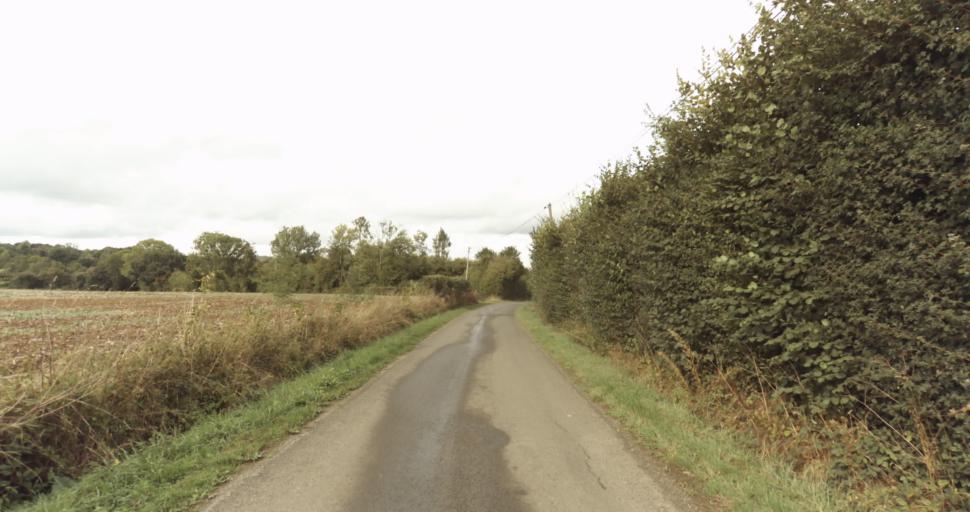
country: FR
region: Lower Normandy
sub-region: Departement de l'Orne
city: Sainte-Gauburge-Sainte-Colombe
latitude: 48.7035
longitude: 0.3688
